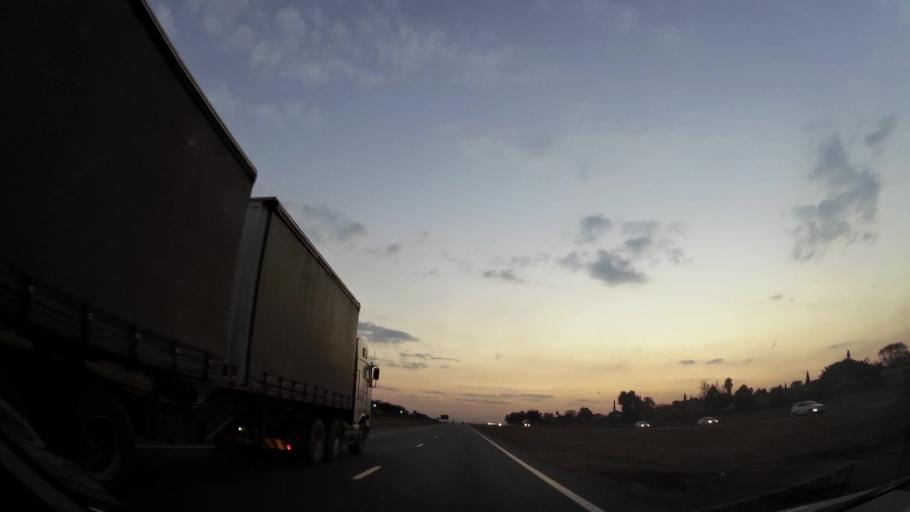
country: ZA
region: Gauteng
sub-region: Ekurhuleni Metropolitan Municipality
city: Boksburg
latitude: -26.2518
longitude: 28.2563
